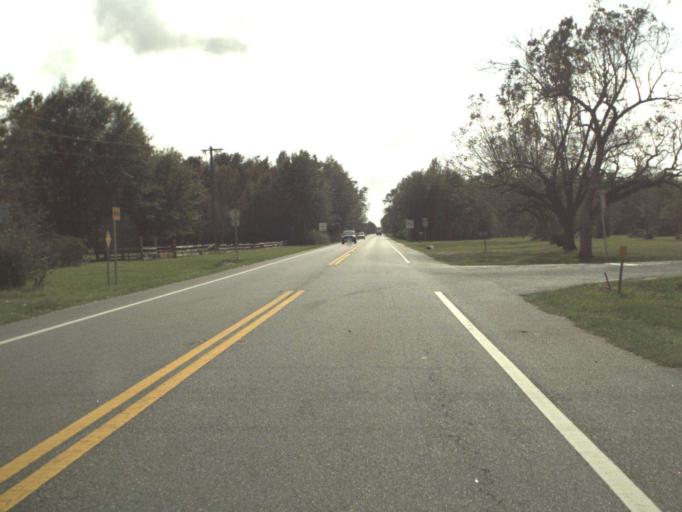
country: US
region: Florida
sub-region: Santa Rosa County
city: Point Baker
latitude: 30.7630
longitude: -87.0422
